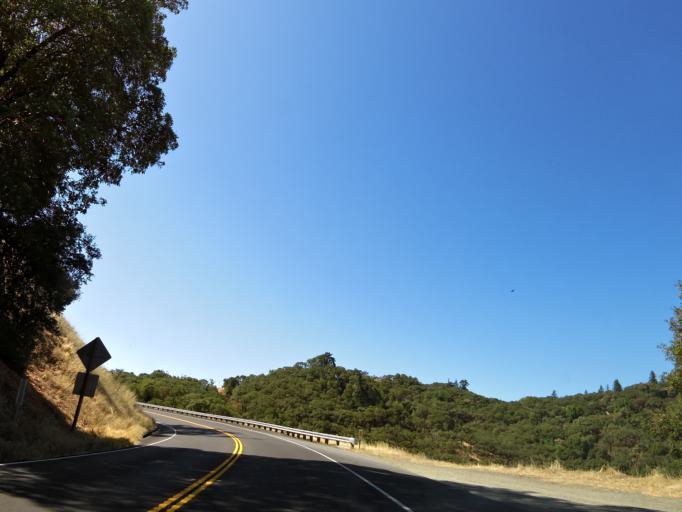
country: US
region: California
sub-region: Mendocino County
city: Boonville
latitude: 38.9756
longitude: -123.3453
